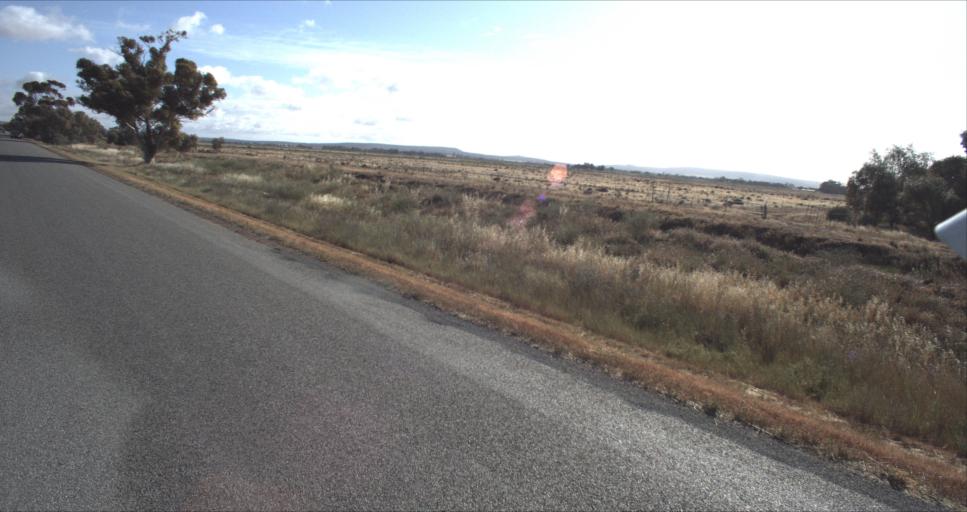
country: AU
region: New South Wales
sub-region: Leeton
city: Leeton
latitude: -34.5190
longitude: 146.3910
